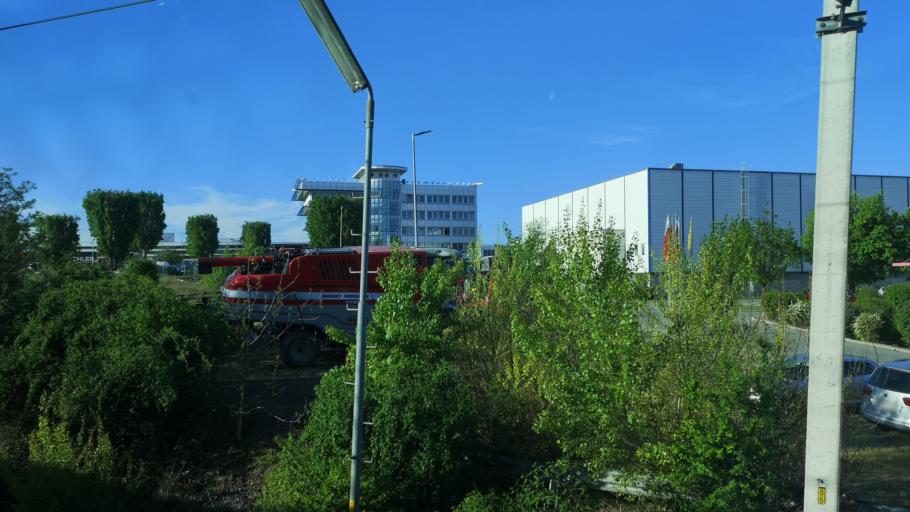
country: AT
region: Lower Austria
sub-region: Politischer Bezirk Wien-Umgebung
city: Schwechat
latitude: 48.1412
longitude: 16.4896
